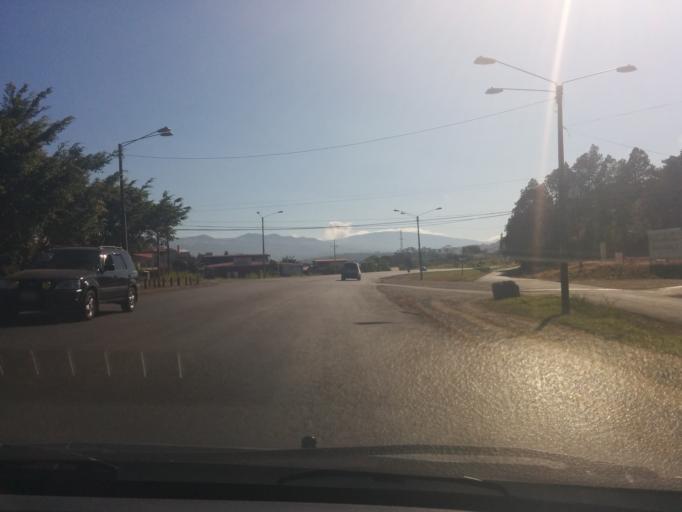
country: CR
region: Alajuela
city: San Rafael
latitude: 10.0753
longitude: -84.4804
